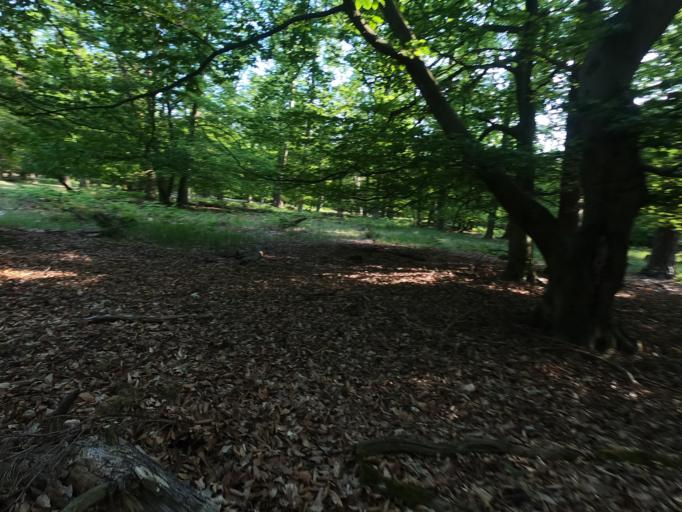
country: DE
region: Hesse
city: Kelsterbach
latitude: 50.0197
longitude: 8.5347
